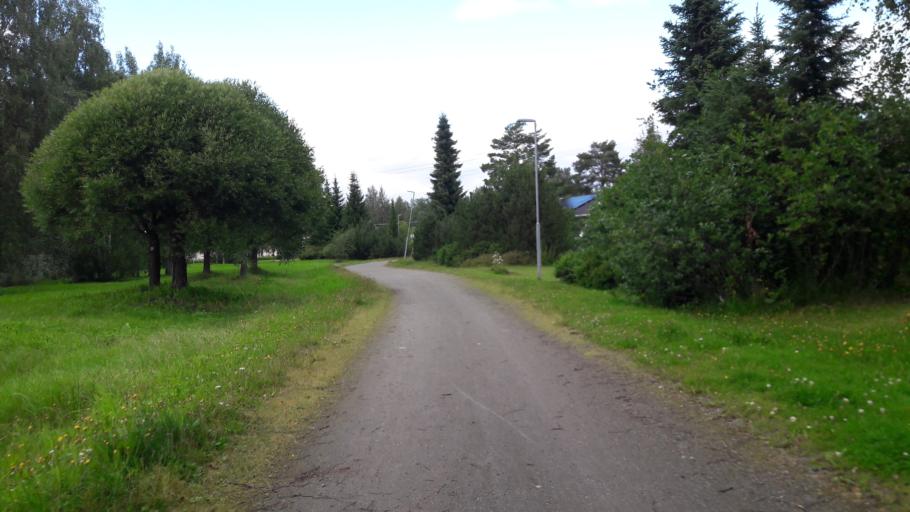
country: FI
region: North Karelia
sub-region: Joensuu
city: Joensuu
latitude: 62.5949
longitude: 29.7957
